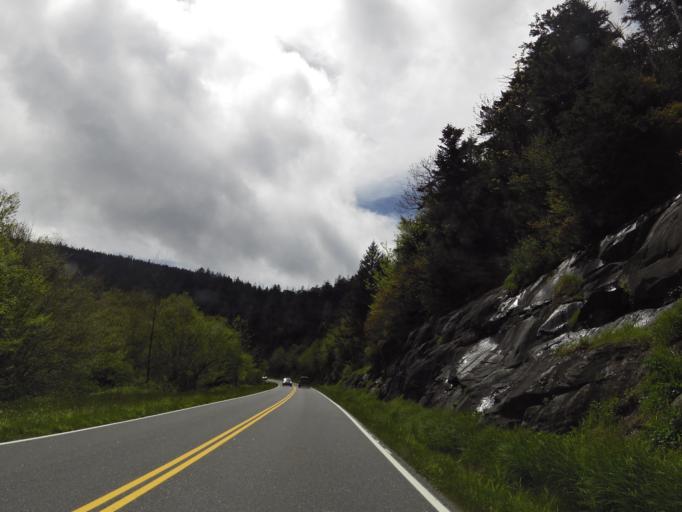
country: US
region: North Carolina
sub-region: Swain County
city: Bryson City
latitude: 35.5654
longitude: -83.4909
